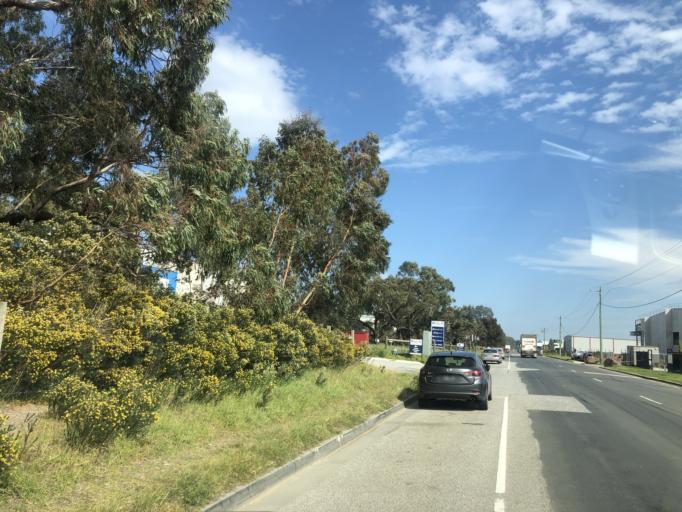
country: AU
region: Victoria
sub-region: Casey
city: Hampton Park
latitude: -38.0359
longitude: 145.2286
